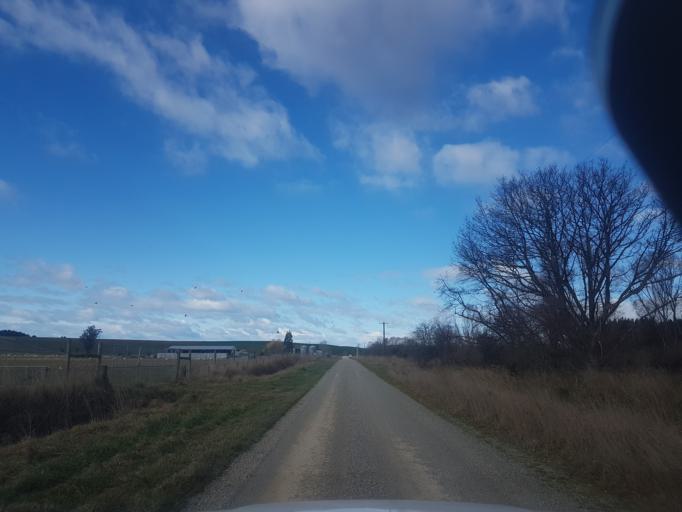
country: NZ
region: Canterbury
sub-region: Timaru District
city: Pleasant Point
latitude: -44.1906
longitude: 171.1981
